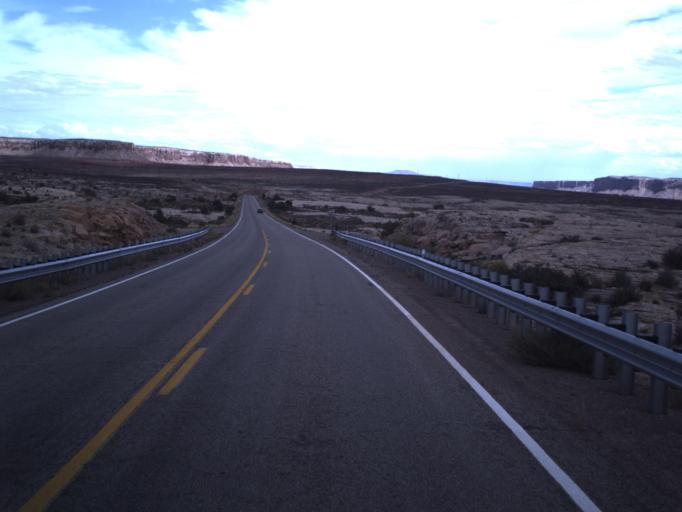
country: US
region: Utah
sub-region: San Juan County
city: Blanding
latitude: 37.2600
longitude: -109.6665
